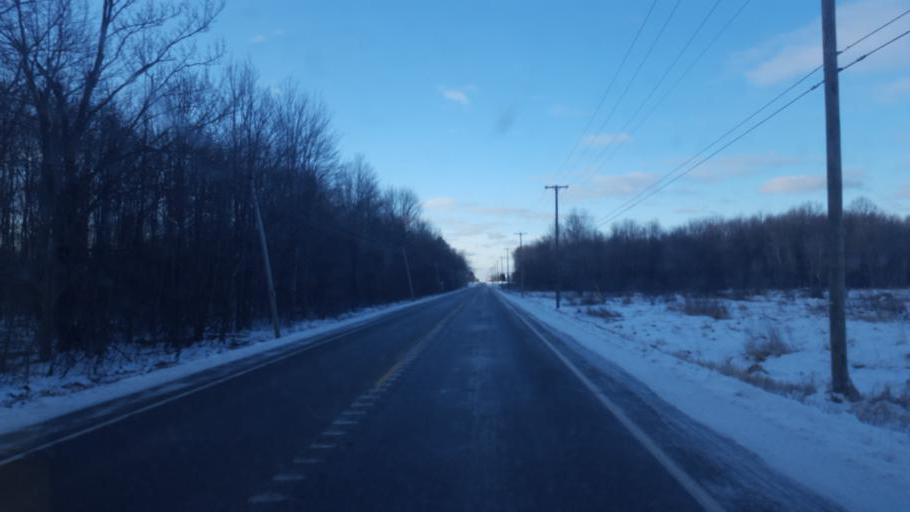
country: US
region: Pennsylvania
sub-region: Mercer County
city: Stoneboro
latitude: 41.3677
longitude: -80.2213
